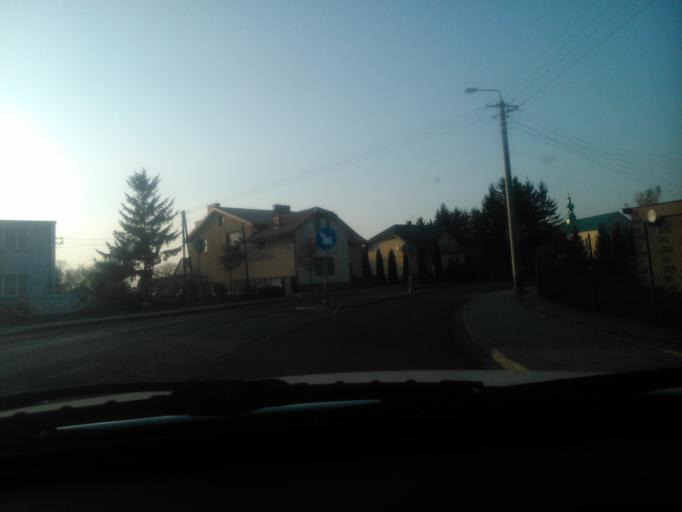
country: PL
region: Masovian Voivodeship
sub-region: Powiat mlawski
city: Szydlowo
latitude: 53.0799
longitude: 20.4486
